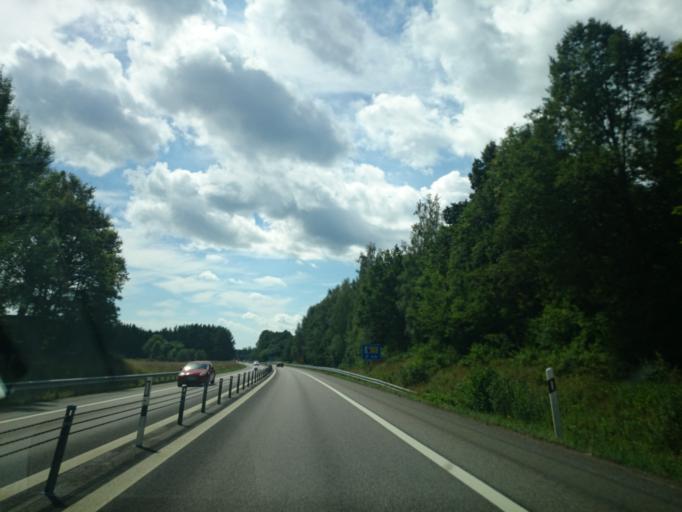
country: SE
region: Kalmar
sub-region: Monsteras Kommun
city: Timmernabben
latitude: 56.9633
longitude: 16.3915
